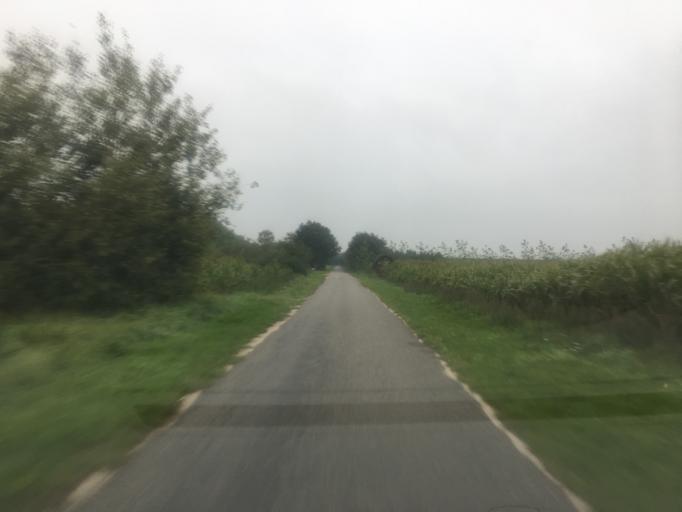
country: DK
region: South Denmark
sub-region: Tonder Kommune
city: Logumkloster
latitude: 55.0405
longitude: 8.9238
